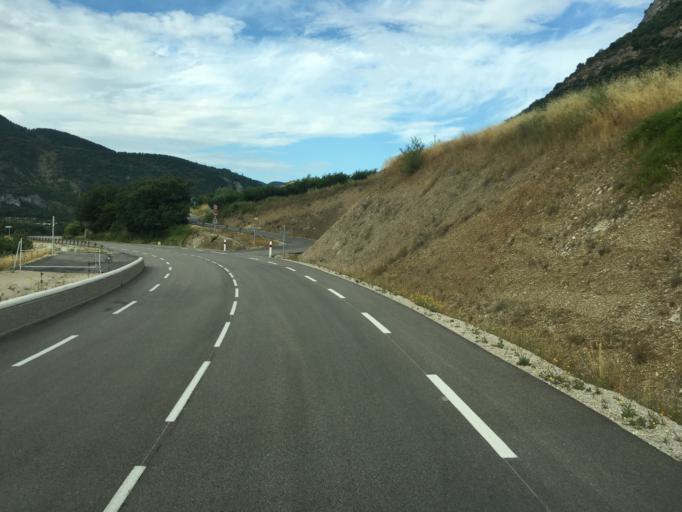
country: FR
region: Rhone-Alpes
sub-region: Departement de la Drome
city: Nyons
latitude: 44.4082
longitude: 5.2523
